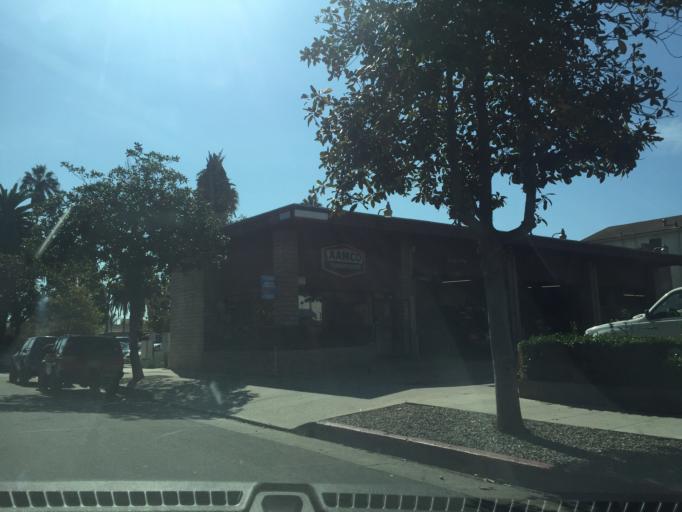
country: US
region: California
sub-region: Santa Barbara County
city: Santa Barbara
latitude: 34.4170
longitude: -119.6930
